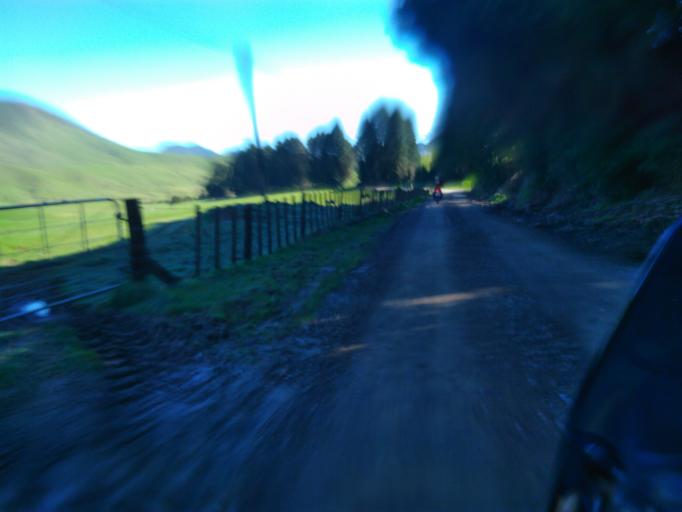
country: NZ
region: Bay of Plenty
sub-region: Opotiki District
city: Opotiki
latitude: -38.3128
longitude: 177.5679
